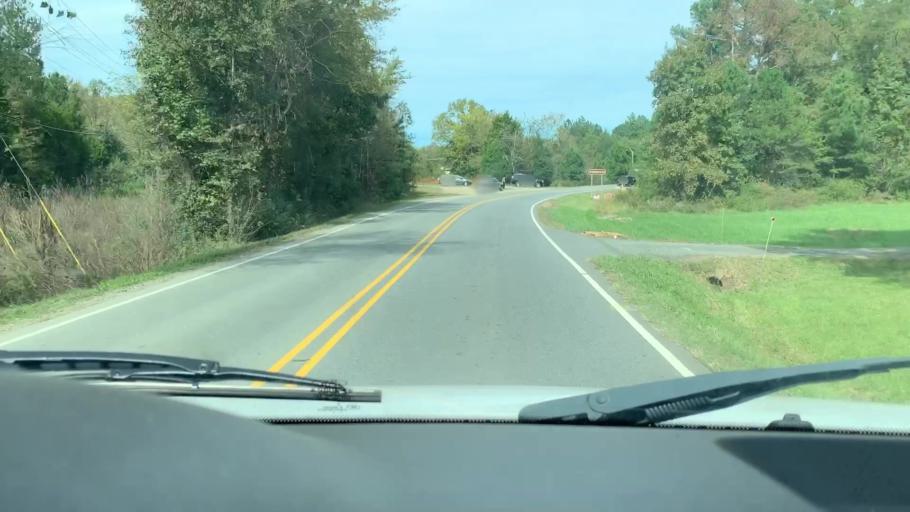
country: US
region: North Carolina
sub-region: Mecklenburg County
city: Huntersville
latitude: 35.4377
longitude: -80.7645
